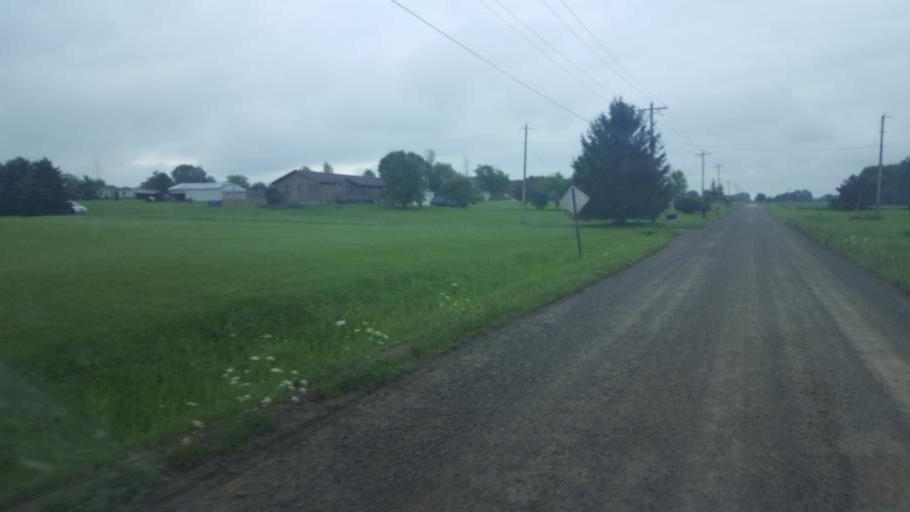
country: US
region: Ohio
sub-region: Knox County
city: Centerburg
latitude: 40.4220
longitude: -82.7432
